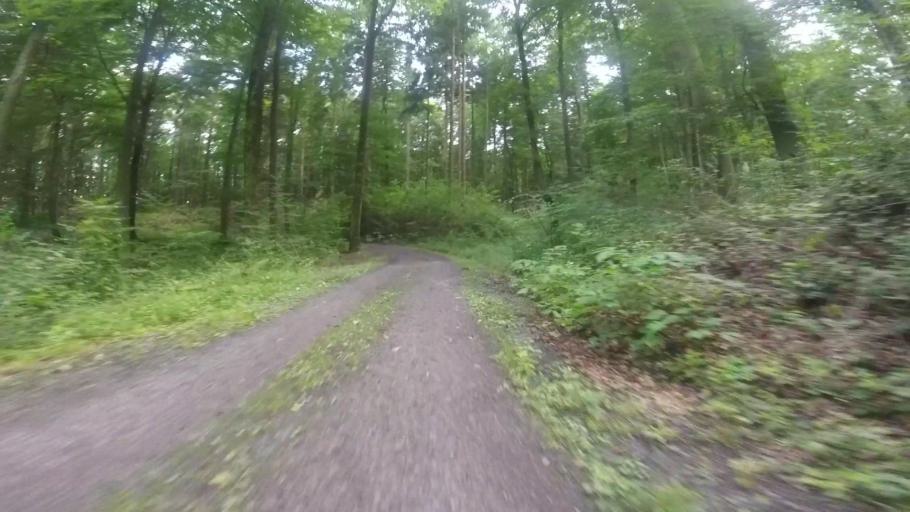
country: DE
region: Baden-Wuerttemberg
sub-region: Regierungsbezirk Stuttgart
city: Beilstein
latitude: 49.0474
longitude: 9.3260
